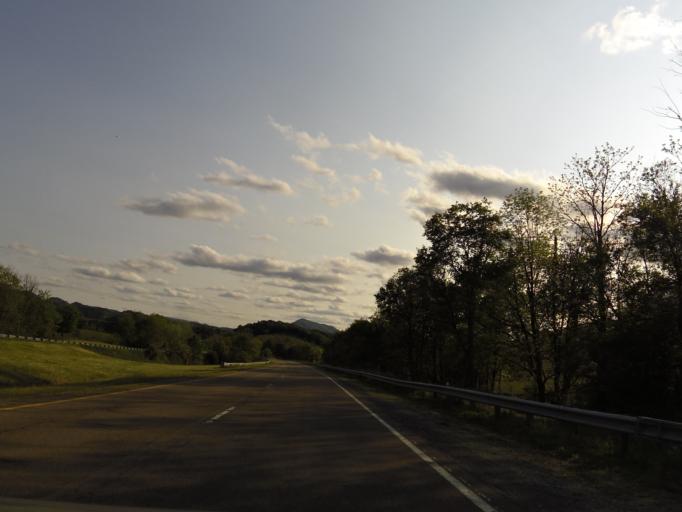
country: US
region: Virginia
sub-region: Tazewell County
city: Tazewell
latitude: 37.1418
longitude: -81.5108
